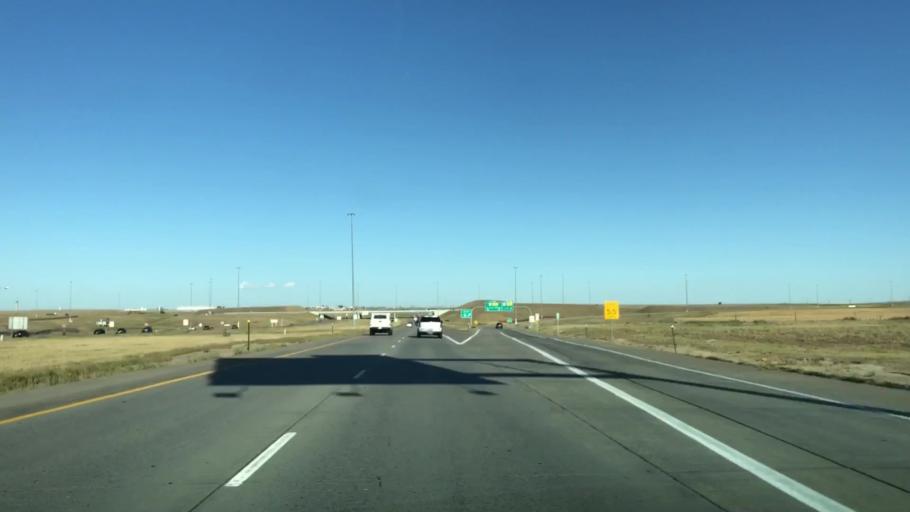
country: US
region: Colorado
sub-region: Adams County
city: Aurora
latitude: 39.8339
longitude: -104.7590
